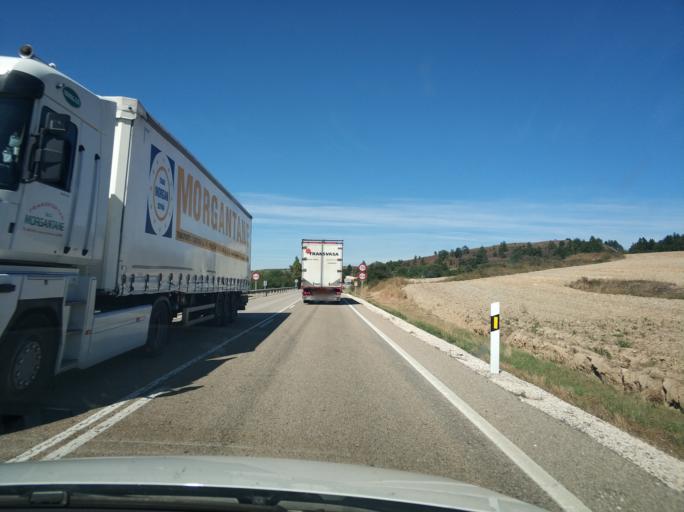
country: ES
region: Castille and Leon
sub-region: Provincia de Burgos
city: Montorio
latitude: 42.6141
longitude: -3.8152
